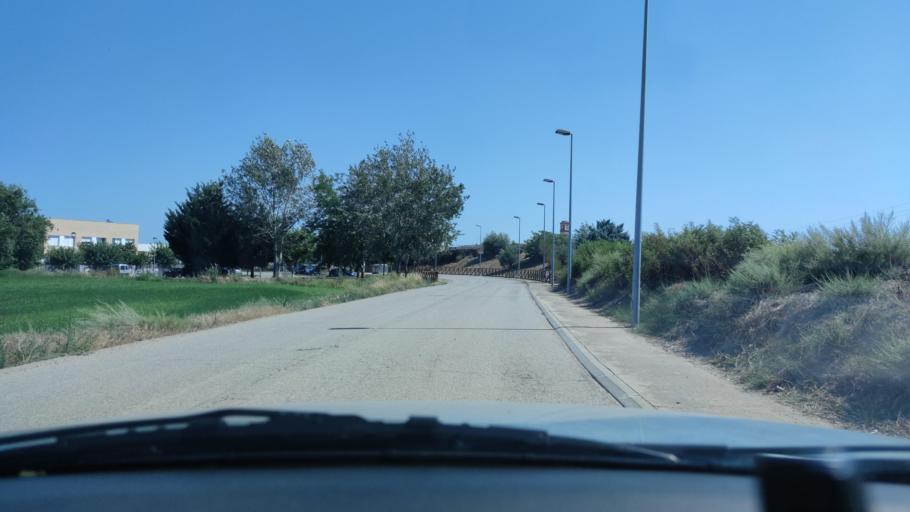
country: ES
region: Catalonia
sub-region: Provincia de Lleida
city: Torrefarrera
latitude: 41.6758
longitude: 0.6305
